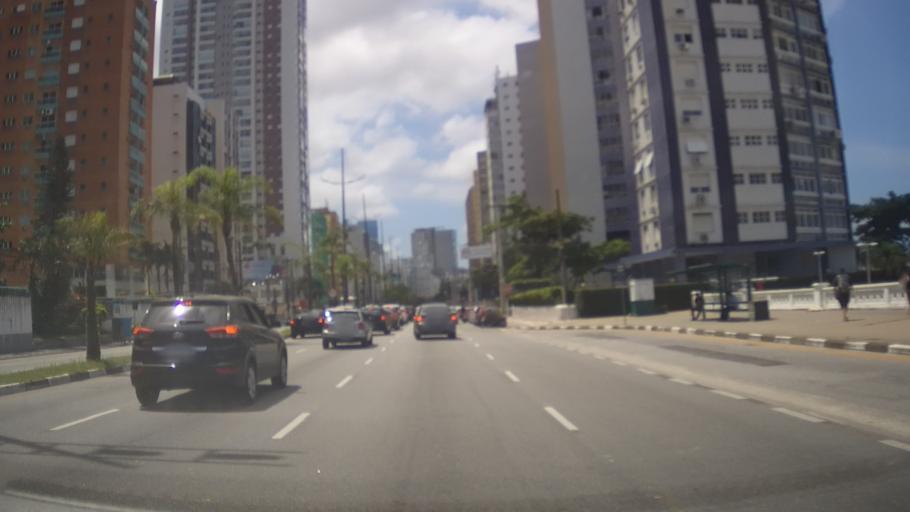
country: BR
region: Sao Paulo
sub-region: Santos
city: Santos
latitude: -23.9688
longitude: -46.3558
